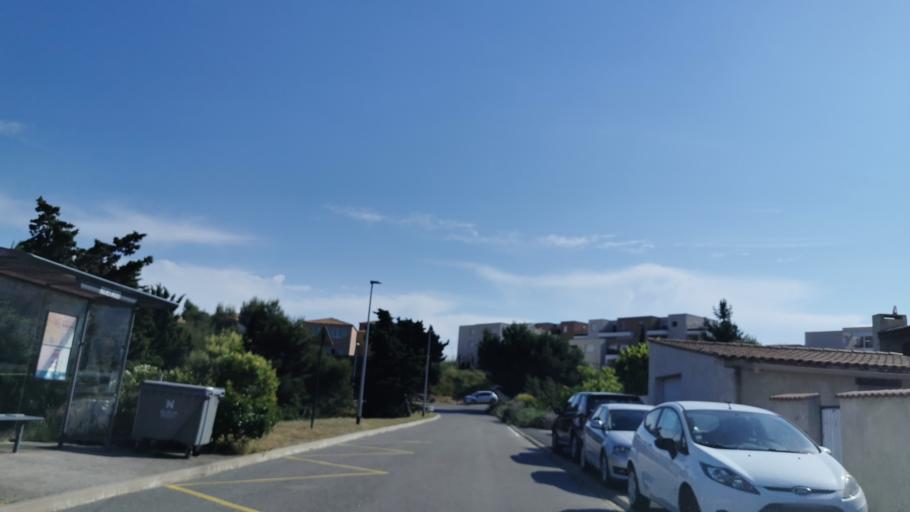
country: FR
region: Languedoc-Roussillon
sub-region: Departement de l'Aude
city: Narbonne
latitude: 43.1412
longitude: 2.9670
